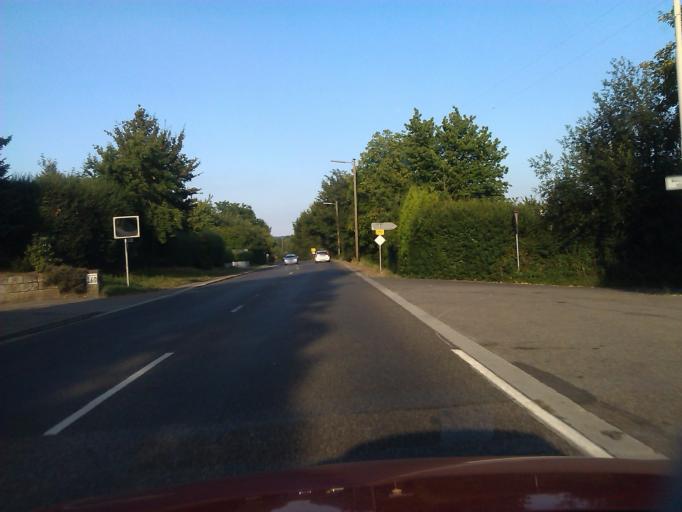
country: DE
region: Baden-Wuerttemberg
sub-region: Regierungsbezirk Stuttgart
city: Heilbronn
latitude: 49.1398
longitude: 9.1711
